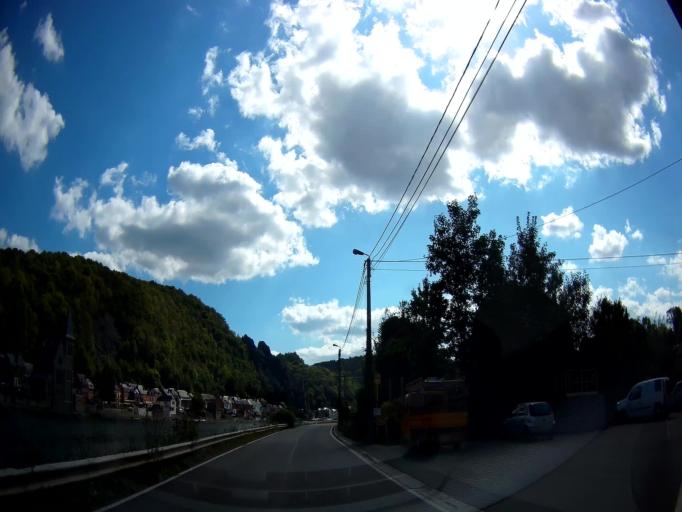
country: BE
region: Wallonia
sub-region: Province de Namur
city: Dinant
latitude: 50.2482
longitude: 4.9184
